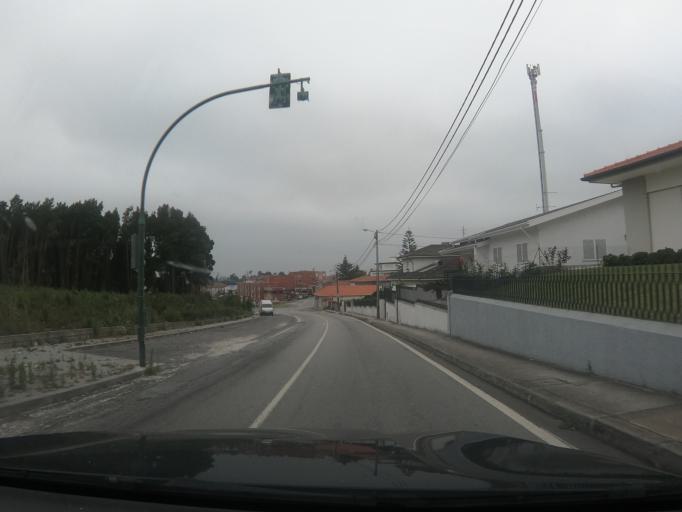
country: PT
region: Aveiro
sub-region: Santa Maria da Feira
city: Pacos de Brandao
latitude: 40.9862
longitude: -8.5894
